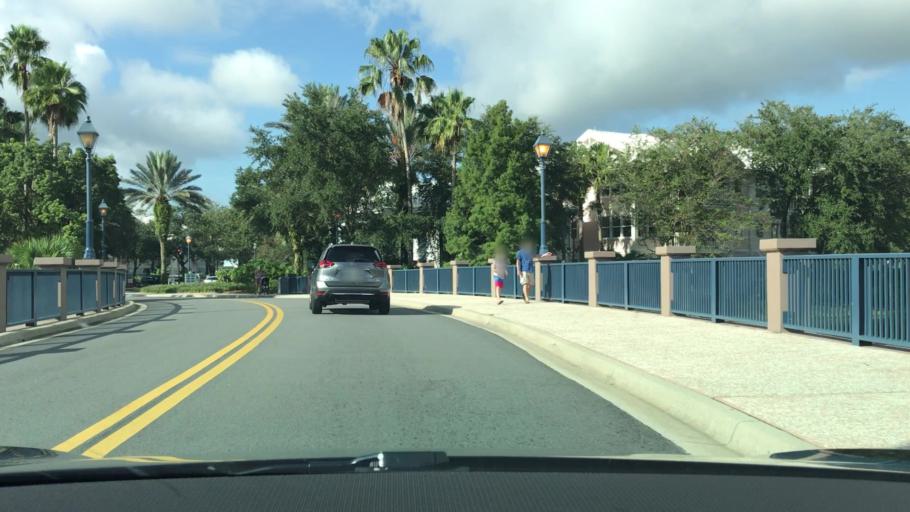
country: US
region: Florida
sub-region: Osceola County
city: Celebration
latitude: 28.3751
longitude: -81.5341
